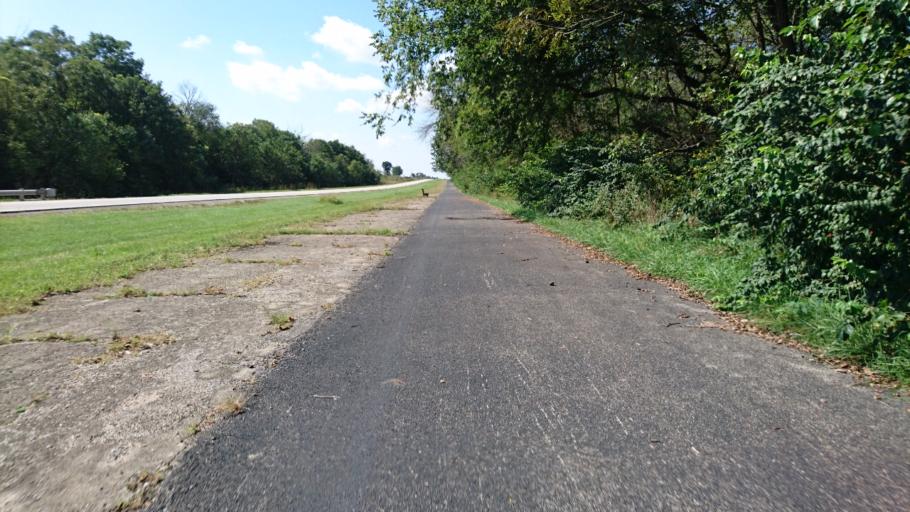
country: US
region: Illinois
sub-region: McLean County
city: Lexington
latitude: 40.6317
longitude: -88.8002
